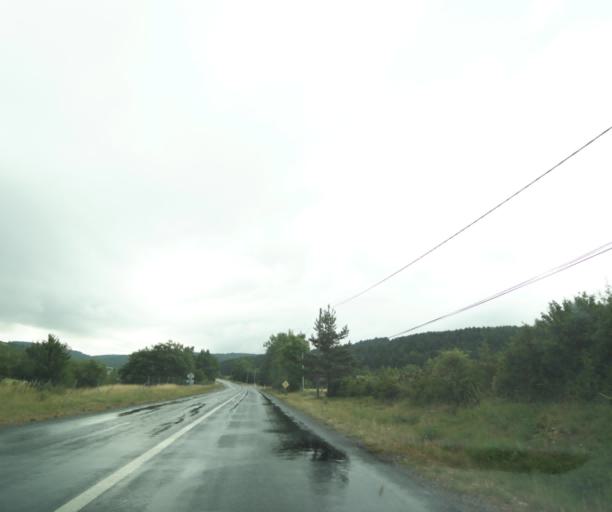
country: FR
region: Midi-Pyrenees
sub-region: Departement de l'Aveyron
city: Severac-le-Chateau
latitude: 44.3825
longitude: 3.1160
